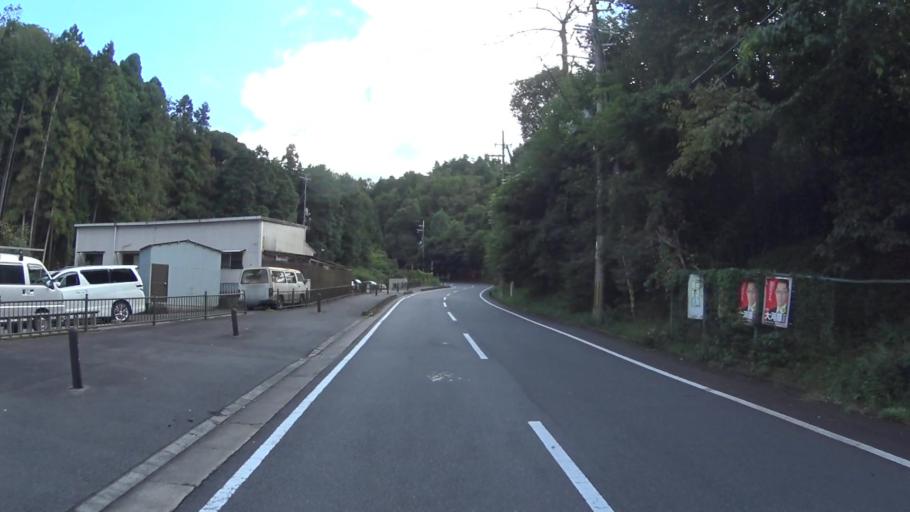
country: JP
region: Kyoto
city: Uji
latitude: 34.9259
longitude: 135.8177
